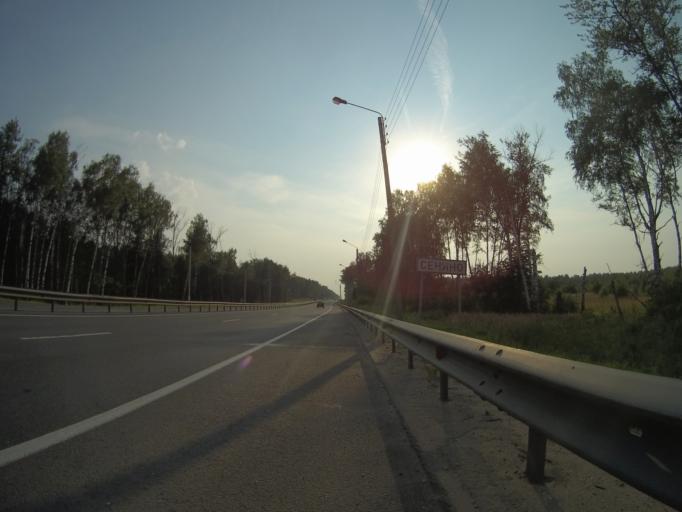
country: RU
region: Vladimir
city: Melekhovo
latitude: 56.2101
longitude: 41.2775
